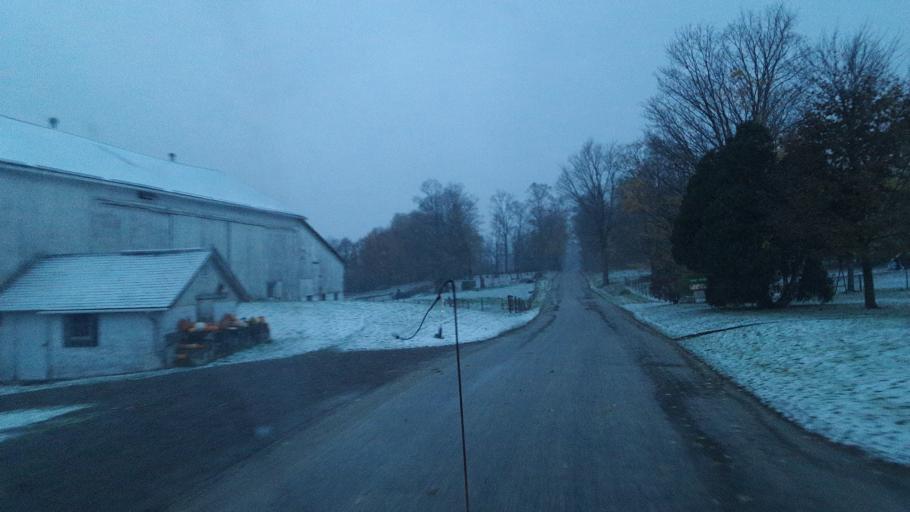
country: US
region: Ohio
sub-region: Geauga County
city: Middlefield
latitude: 41.4098
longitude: -81.1017
